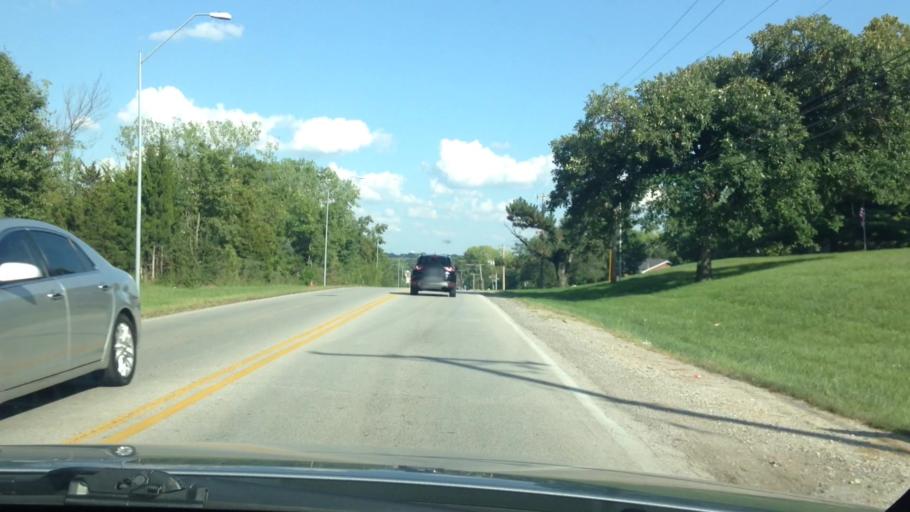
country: US
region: Missouri
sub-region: Jackson County
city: Grandview
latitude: 38.8904
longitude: -94.5998
